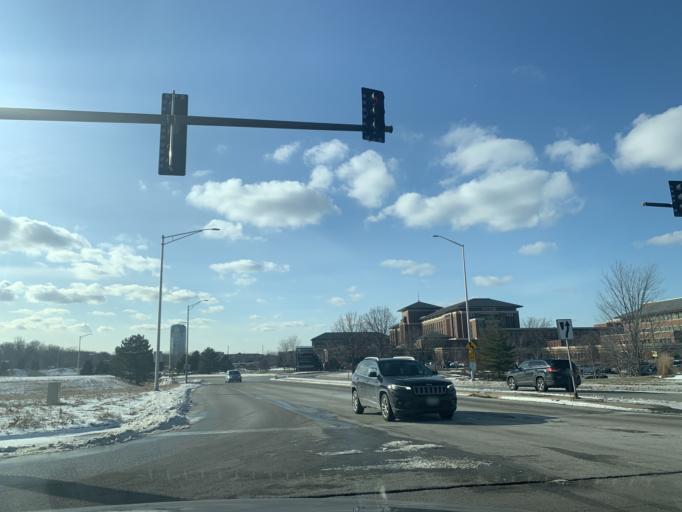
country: US
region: Illinois
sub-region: DuPage County
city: Oak Brook
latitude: 41.8631
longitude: -87.9314
